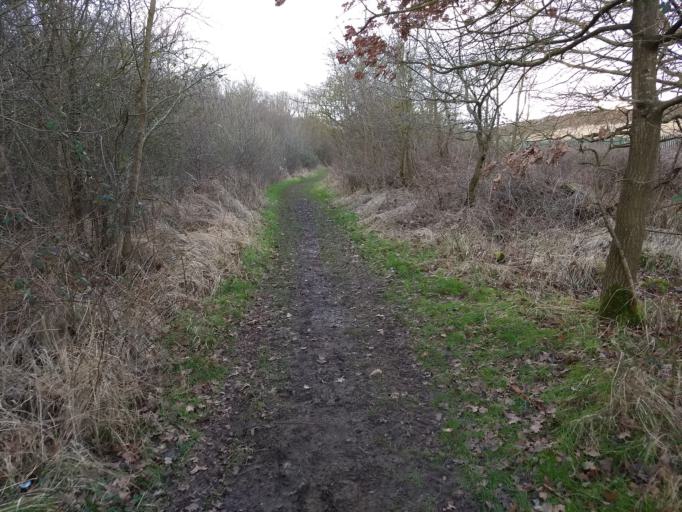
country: GB
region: England
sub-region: Buckinghamshire
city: Bletchley
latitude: 51.9872
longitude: -0.7402
